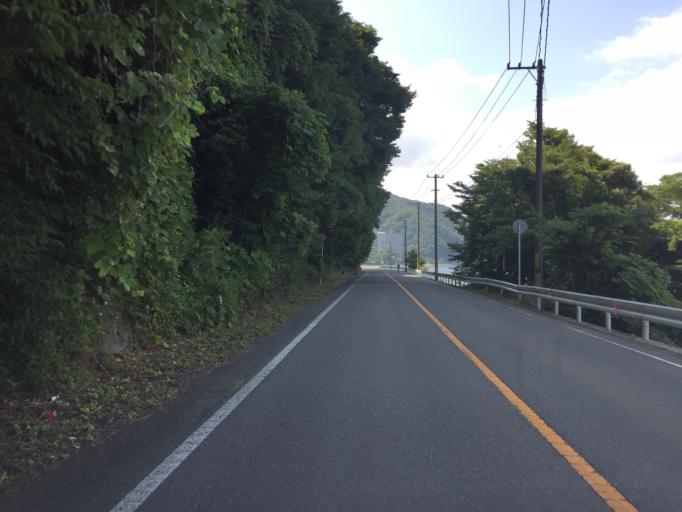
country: JP
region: Fukushima
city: Inawashiro
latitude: 37.4691
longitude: 140.1529
